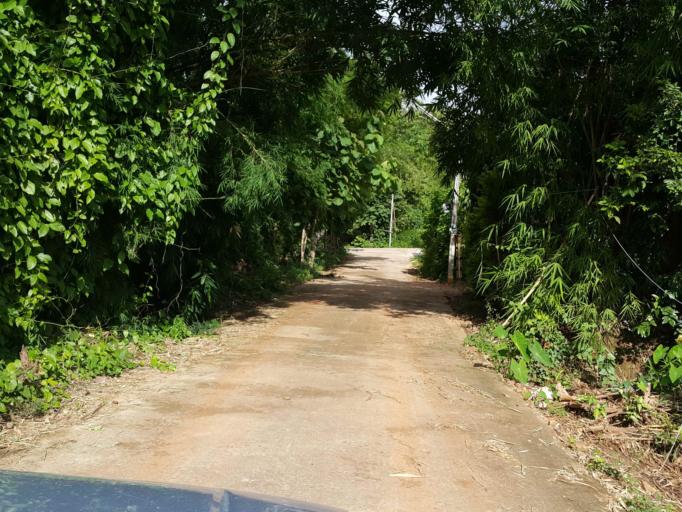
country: TH
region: Chiang Mai
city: Mae Chaem
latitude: 18.4886
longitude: 98.3798
